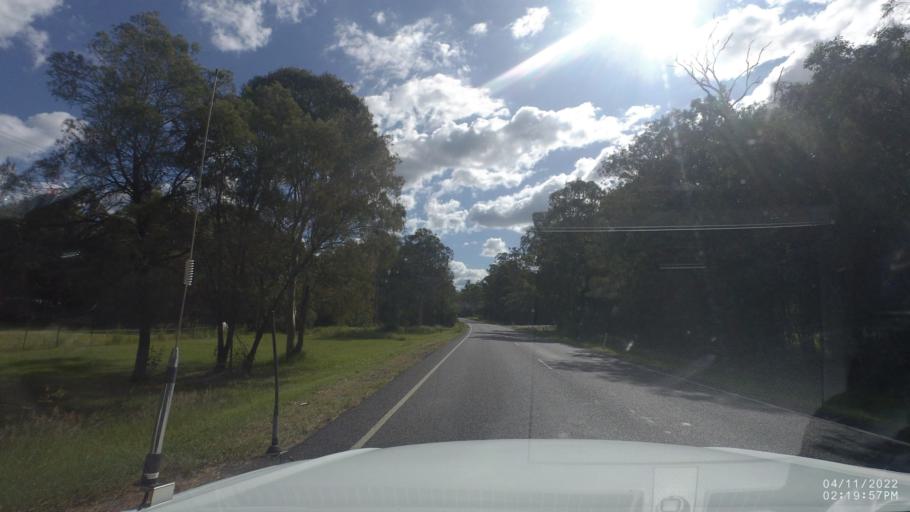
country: AU
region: Queensland
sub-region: Logan
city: Chambers Flat
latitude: -27.7698
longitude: 153.1333
